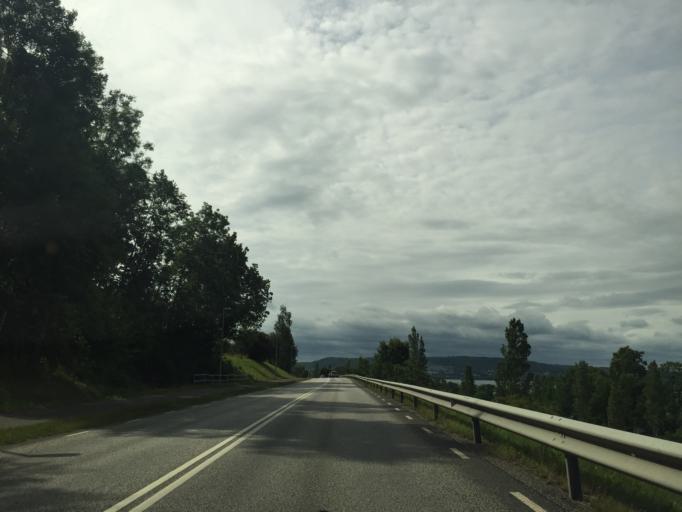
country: SE
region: Joenkoeping
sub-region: Jonkopings Kommun
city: Kaxholmen
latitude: 57.8256
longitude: 14.2705
